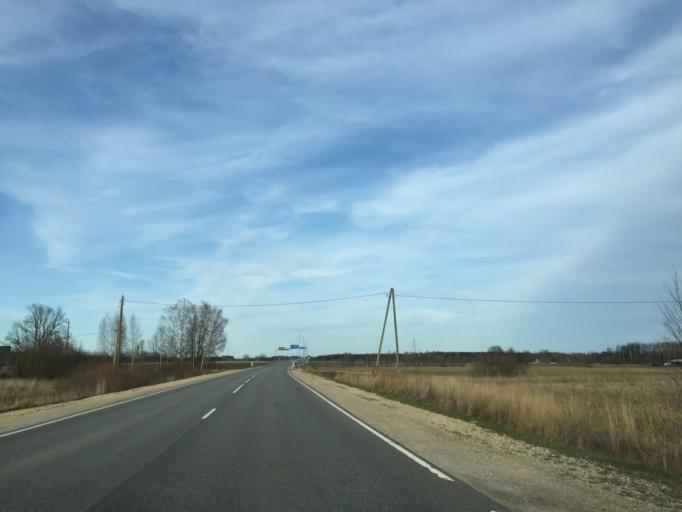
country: LV
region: Lielvarde
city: Lielvarde
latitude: 56.8034
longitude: 24.8720
